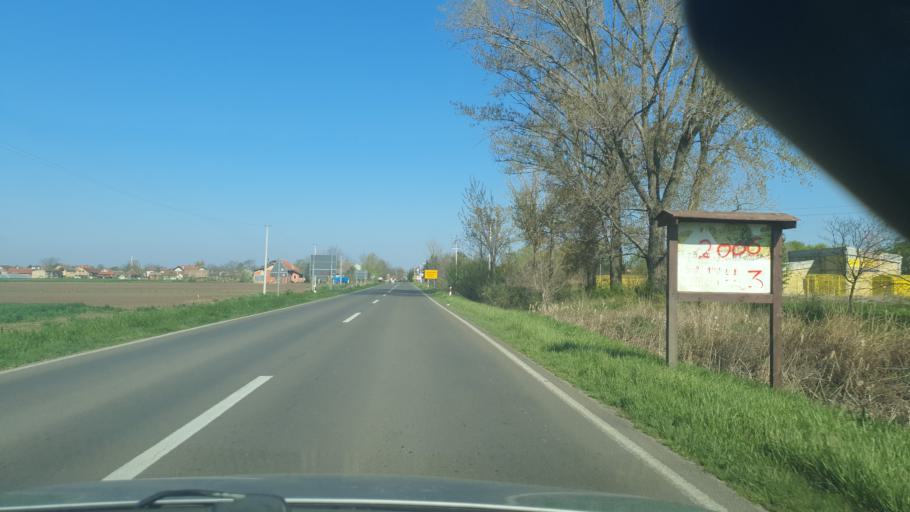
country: RS
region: Autonomna Pokrajina Vojvodina
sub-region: Zapadnobacki Okrug
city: Sombor
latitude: 45.7653
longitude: 19.2942
